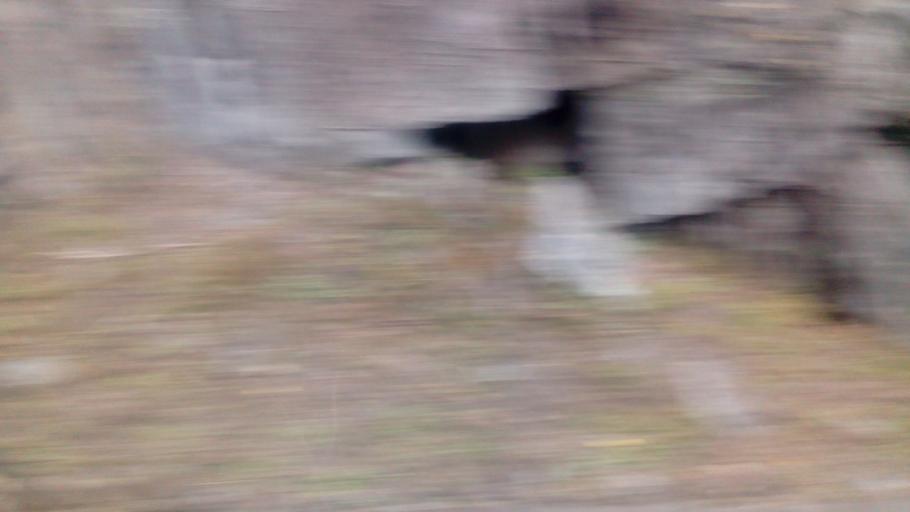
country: TW
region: Taiwan
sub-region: Yilan
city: Yilan
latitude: 24.5652
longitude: 121.4741
